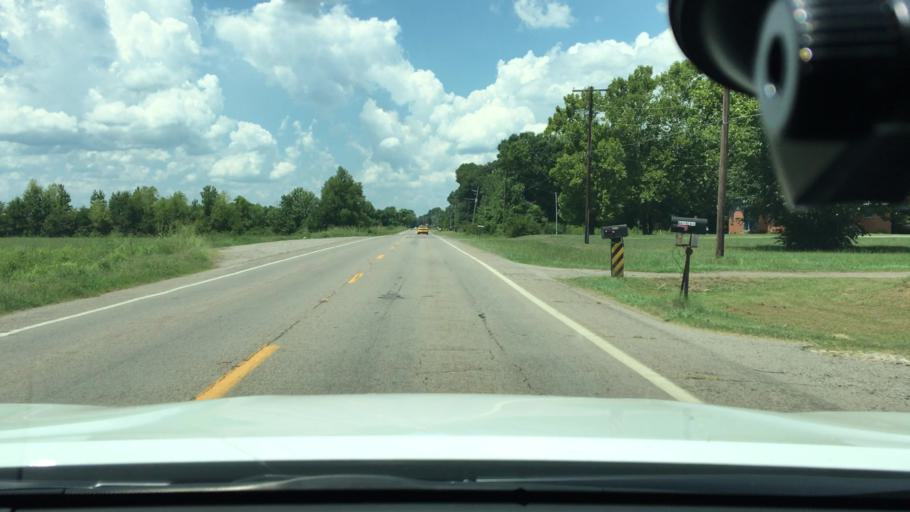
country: US
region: Arkansas
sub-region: Logan County
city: Booneville
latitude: 35.1479
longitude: -93.8711
